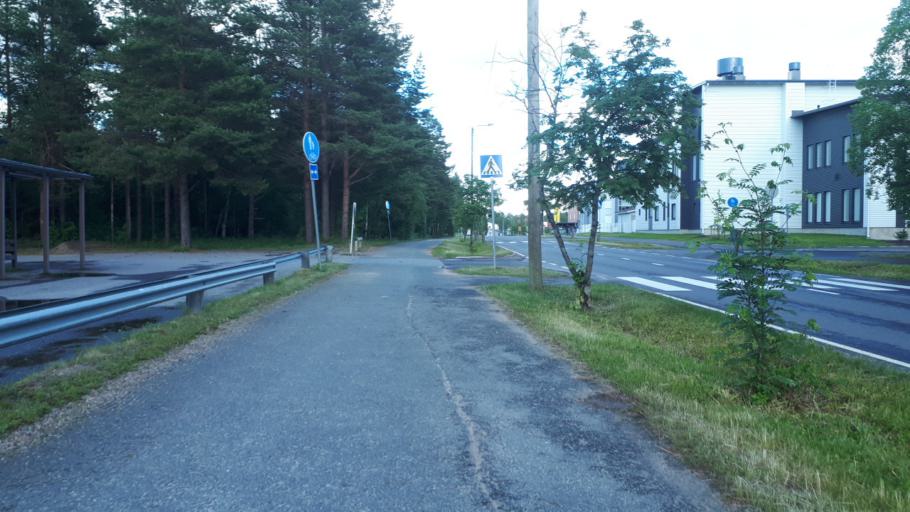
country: FI
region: Northern Ostrobothnia
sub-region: Oulunkaari
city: Ii
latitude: 65.3230
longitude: 25.3706
